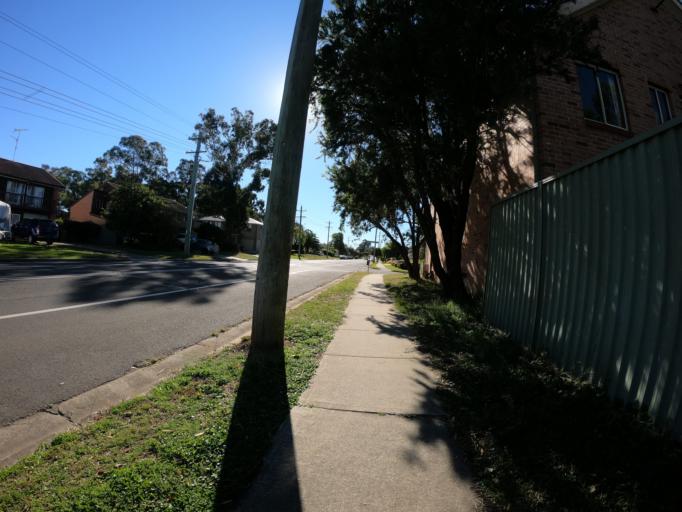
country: AU
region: New South Wales
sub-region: Hawkesbury
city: South Windsor
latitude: -33.6303
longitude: 150.7967
